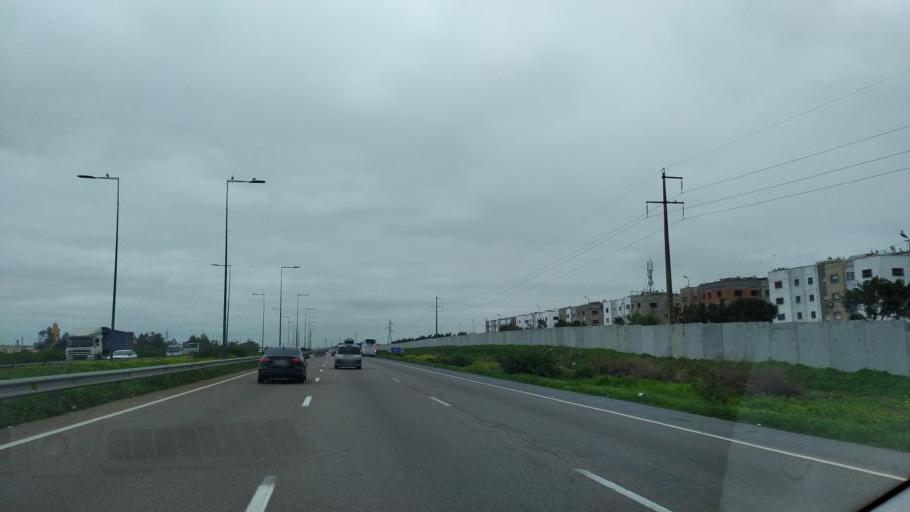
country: MA
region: Grand Casablanca
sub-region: Mohammedia
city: Mohammedia
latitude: 33.6721
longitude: -7.3870
